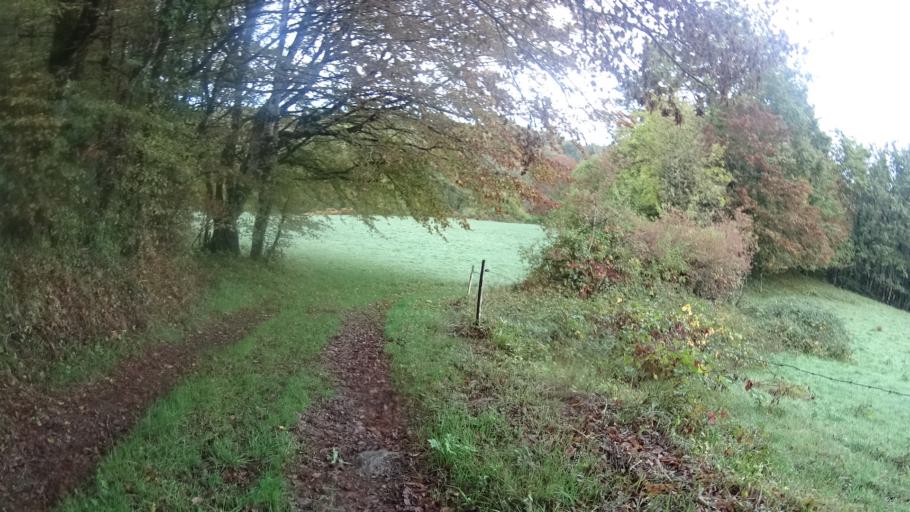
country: FR
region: Aquitaine
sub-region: Departement de la Dordogne
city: Payzac
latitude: 45.3537
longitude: 1.2041
